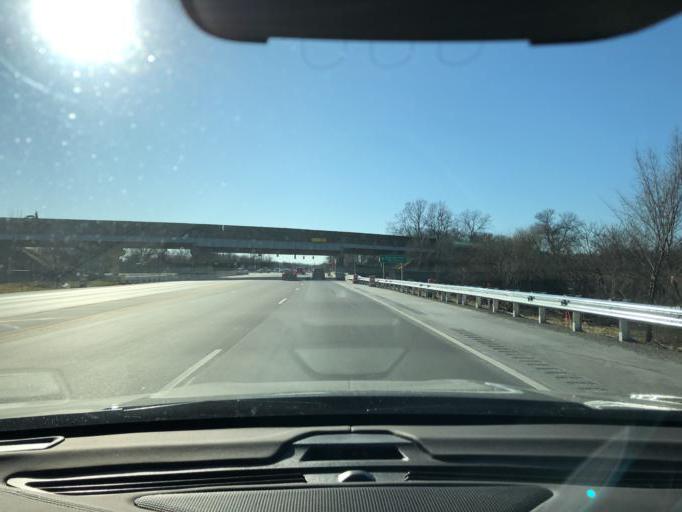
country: US
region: Michigan
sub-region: Washtenaw County
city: Ypsilanti
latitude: 42.2436
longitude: -83.5651
